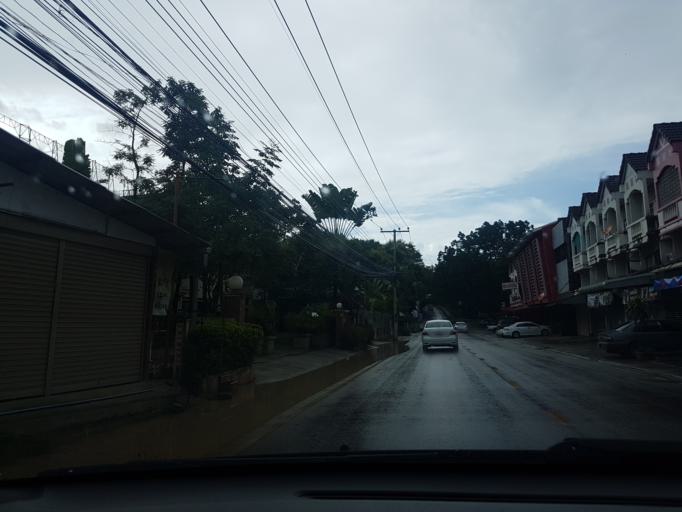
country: TH
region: Lampang
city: Lampang
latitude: 18.2965
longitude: 99.4716
